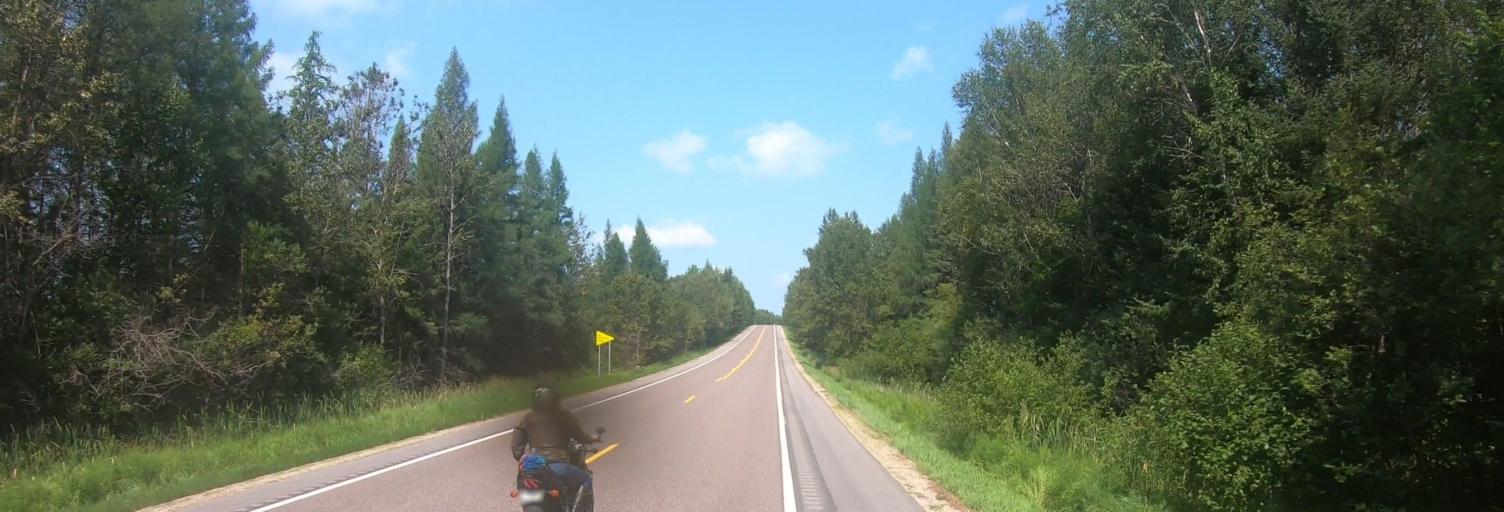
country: US
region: Minnesota
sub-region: Saint Louis County
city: Parkville
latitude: 48.1606
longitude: -92.5254
